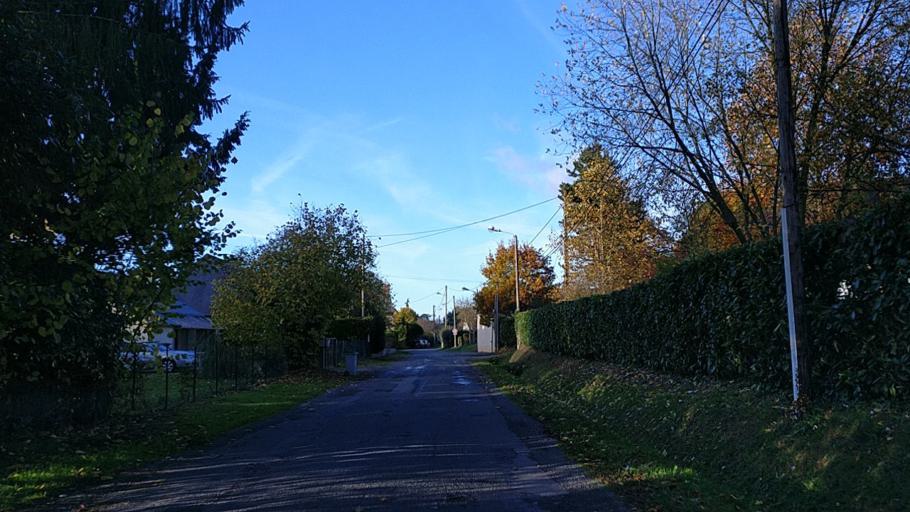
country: FR
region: Brittany
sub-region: Departement d'Ille-et-Vilaine
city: Fouillard
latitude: 48.1347
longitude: -1.5690
